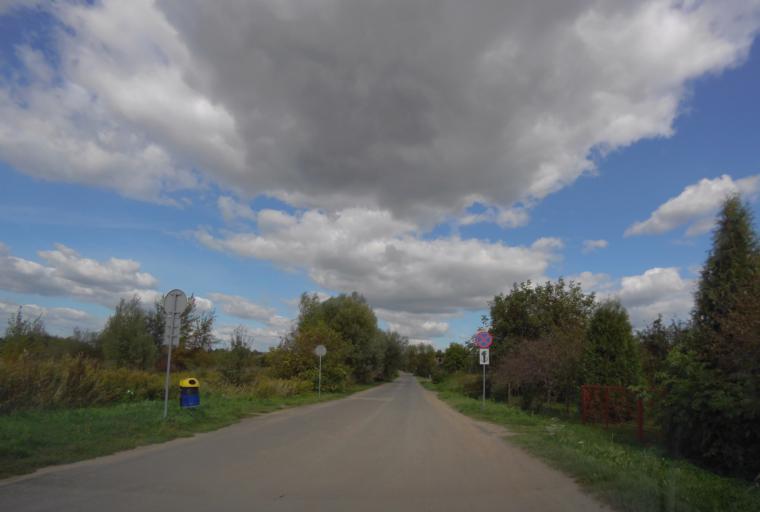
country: PL
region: Subcarpathian Voivodeship
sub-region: Tarnobrzeg
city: Tarnobrzeg
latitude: 50.5512
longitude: 21.6591
